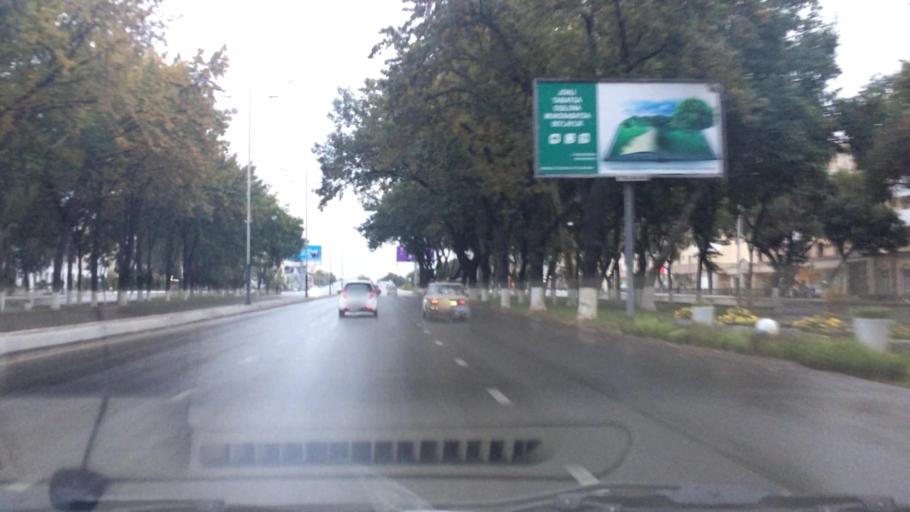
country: UZ
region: Toshkent Shahri
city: Tashkent
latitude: 41.2958
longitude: 69.2275
